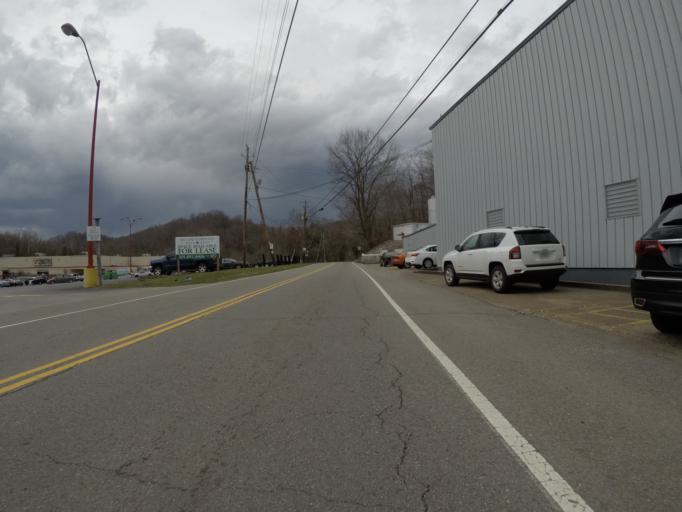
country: US
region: Ohio
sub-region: Lawrence County
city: Burlington
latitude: 38.4203
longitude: -82.5038
